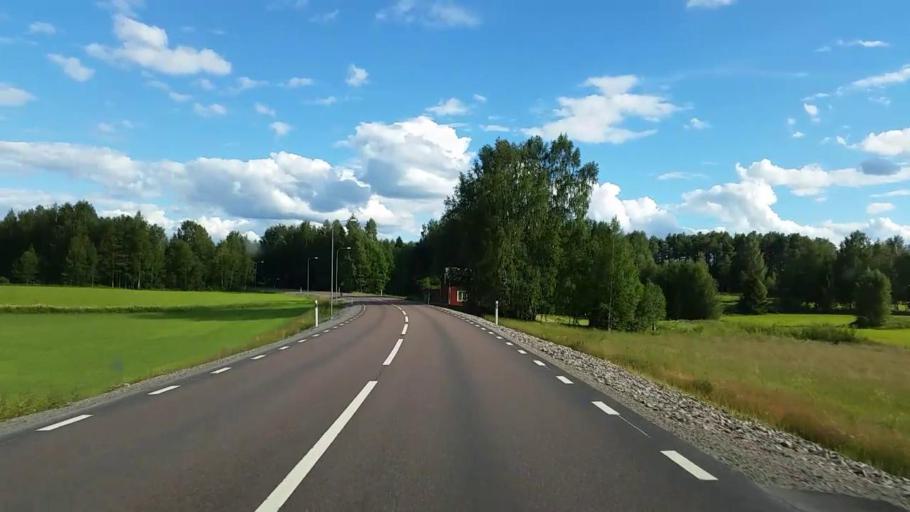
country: SE
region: Gaevleborg
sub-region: Ljusdals Kommun
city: Ljusdal
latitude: 61.8398
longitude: 16.0018
